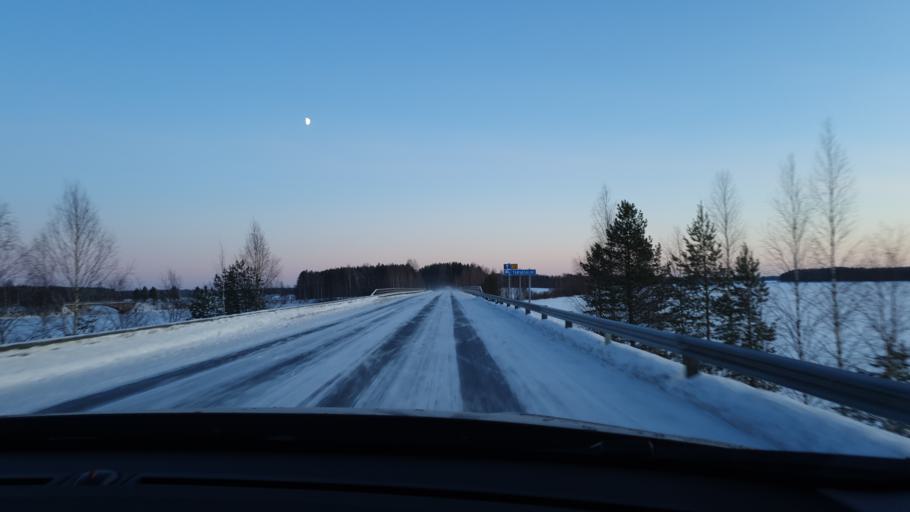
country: FI
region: Kainuu
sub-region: Kehys-Kainuu
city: Kuhmo
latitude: 64.0863
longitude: 29.0896
